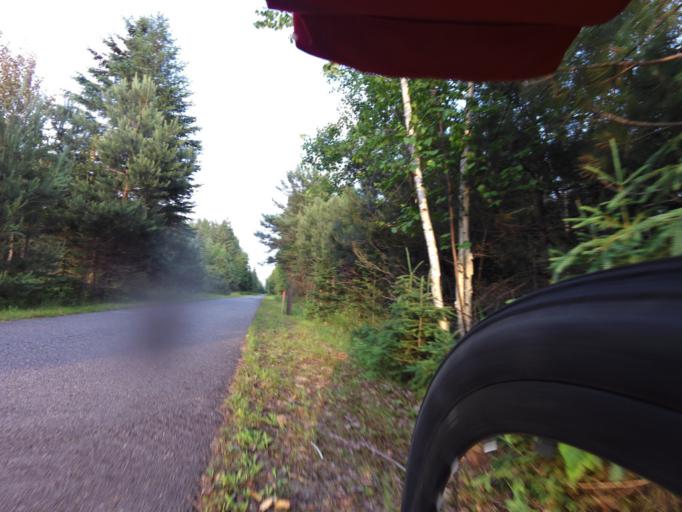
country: CA
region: Quebec
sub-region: Laurentides
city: Riviere-Rouge
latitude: 46.3941
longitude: -75.0264
